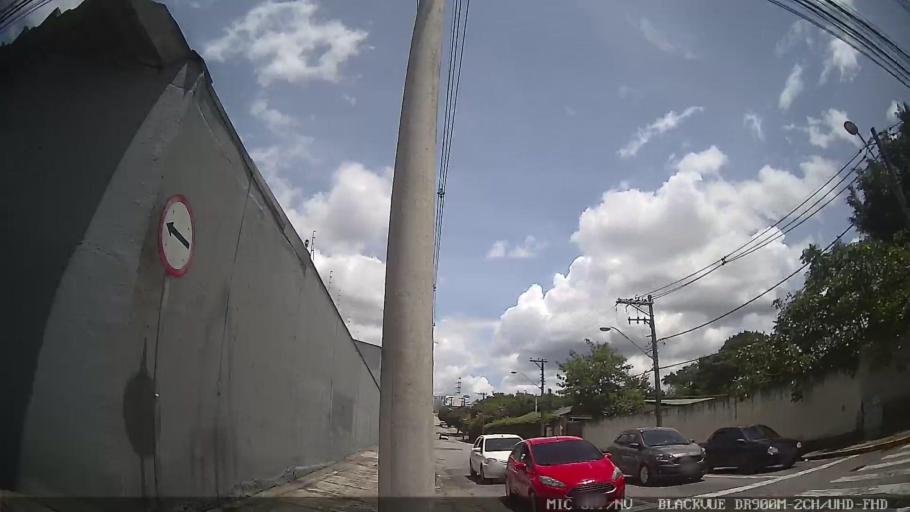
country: BR
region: Sao Paulo
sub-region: Mogi das Cruzes
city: Mogi das Cruzes
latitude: -23.5414
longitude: -46.2327
